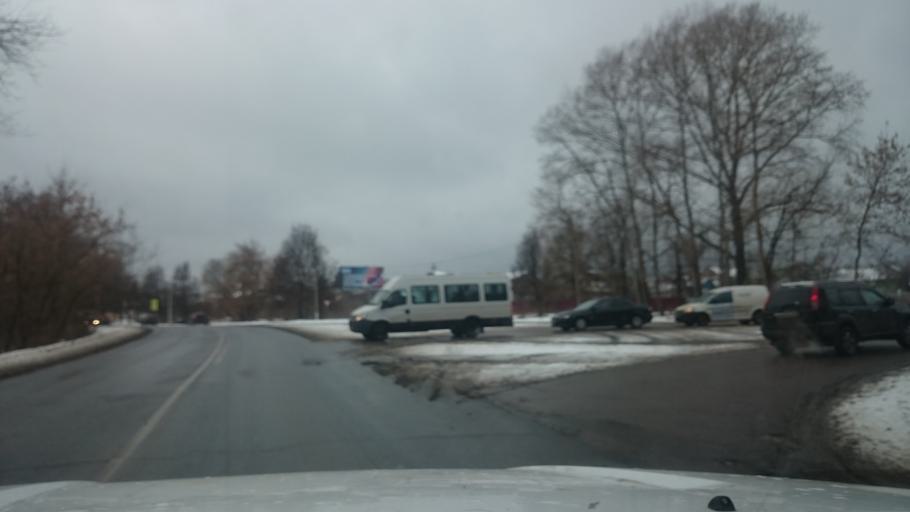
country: RU
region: Tula
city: Kosaya Gora
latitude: 54.1144
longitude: 37.5575
